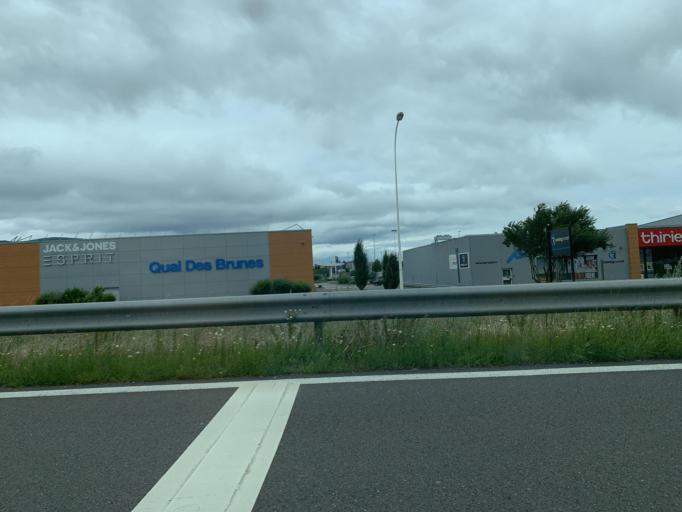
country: FR
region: Alsace
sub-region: Departement du Haut-Rhin
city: Cernay
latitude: 47.7926
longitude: 7.1692
